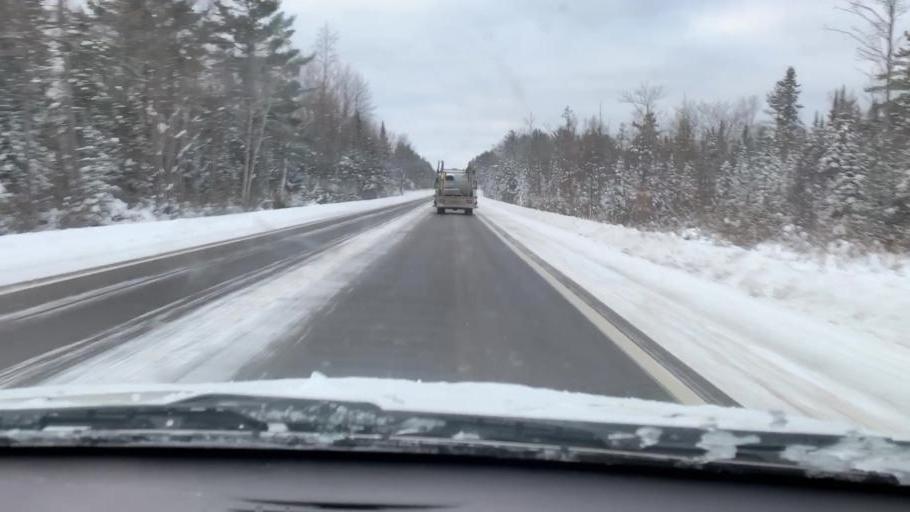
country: US
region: Michigan
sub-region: Kalkaska County
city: Kalkaska
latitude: 44.6984
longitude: -85.2063
